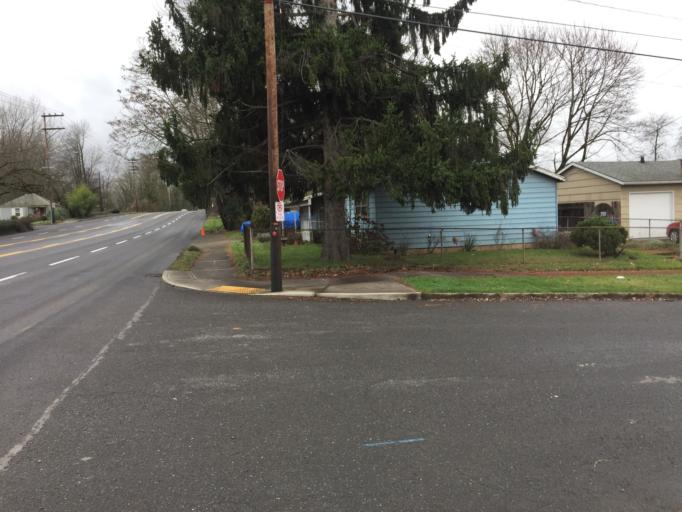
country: US
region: Washington
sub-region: Clark County
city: Vancouver
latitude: 45.5944
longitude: -122.7230
